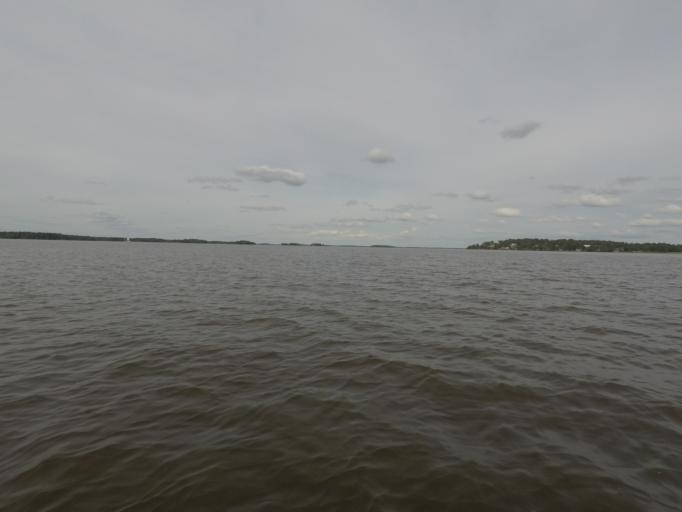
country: SE
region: Soedermanland
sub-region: Eskilstuna Kommun
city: Torshalla
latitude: 59.4579
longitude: 16.4316
